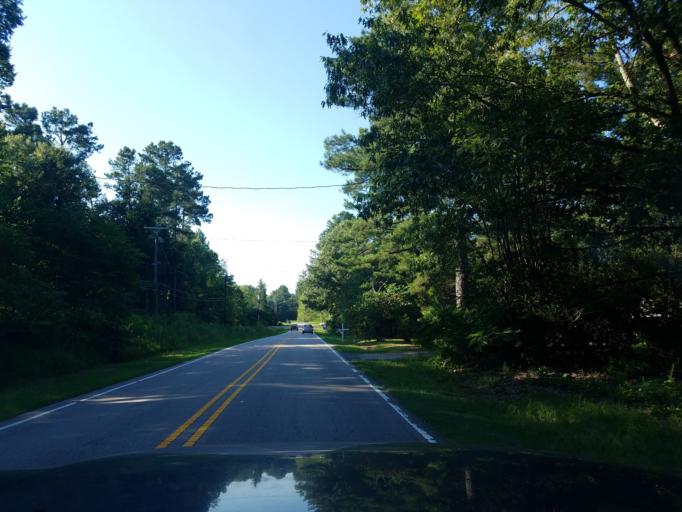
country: US
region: North Carolina
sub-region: Wake County
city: Green Level
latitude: 35.8808
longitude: -78.9152
